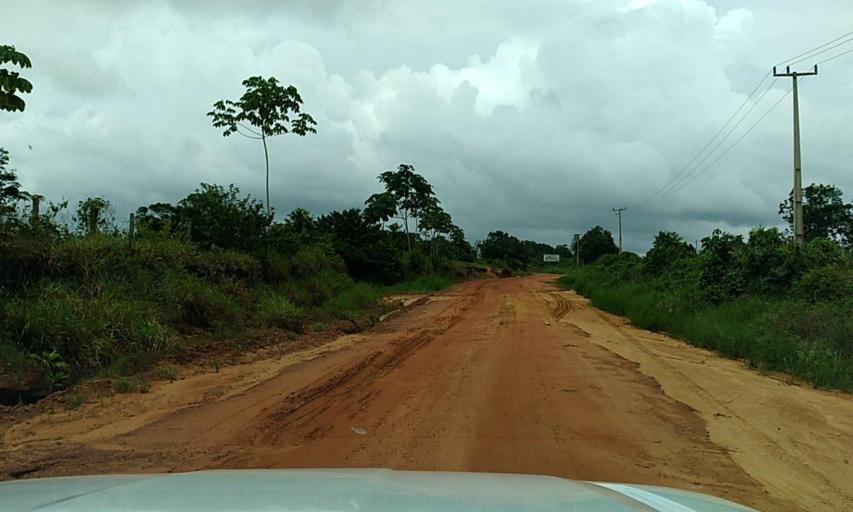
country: BR
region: Para
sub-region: Senador Jose Porfirio
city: Senador Jose Porfirio
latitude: -2.6145
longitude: -51.8729
